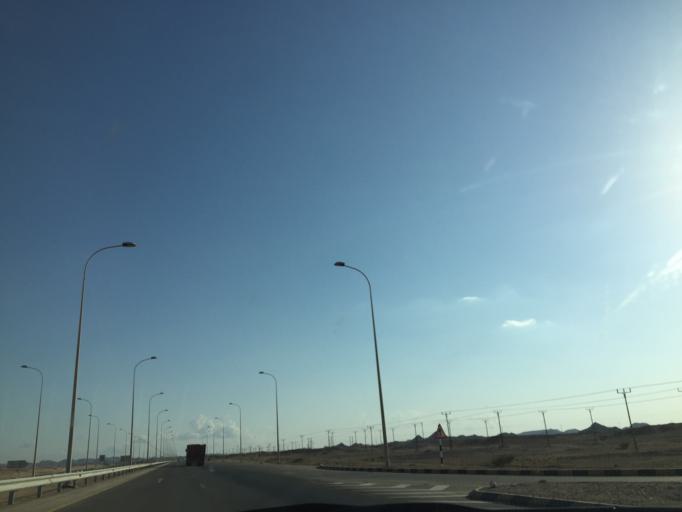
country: OM
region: Zufar
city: Salalah
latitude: 17.5313
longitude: 54.0556
